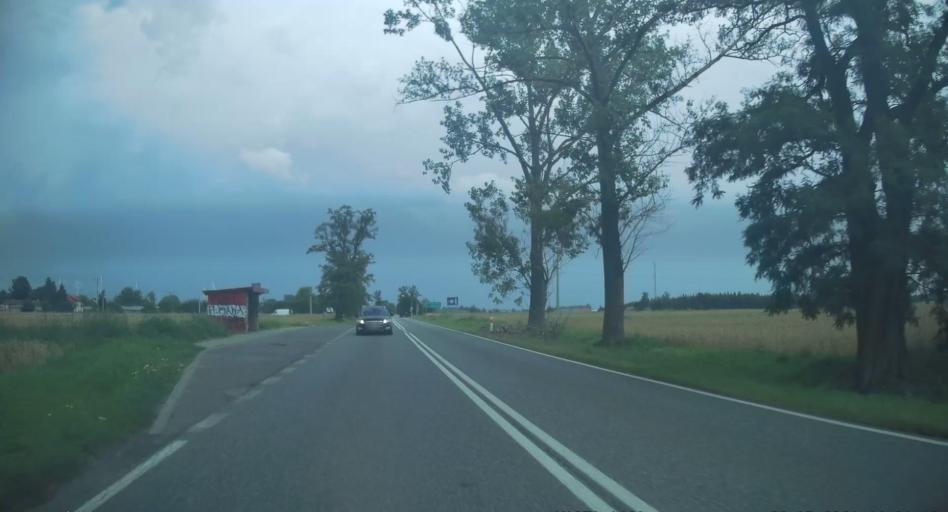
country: PL
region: Lodz Voivodeship
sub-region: Powiat skierniewicki
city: Gluchow
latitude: 51.7766
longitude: 20.1167
